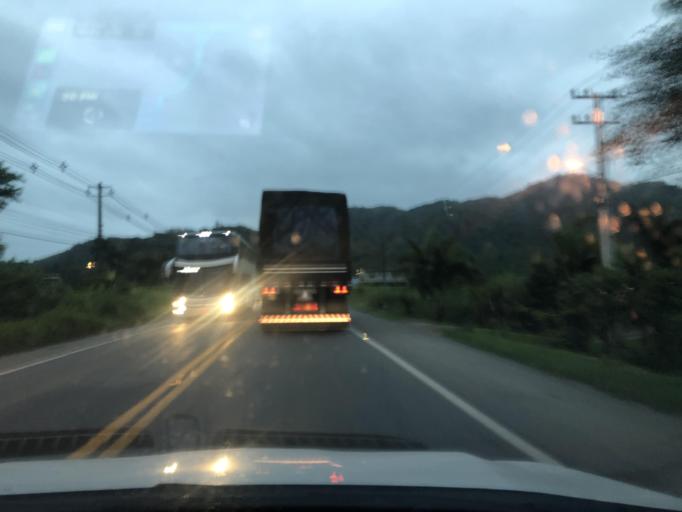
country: BR
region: Santa Catarina
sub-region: Pomerode
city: Pomerode
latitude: -26.7597
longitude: -49.0748
